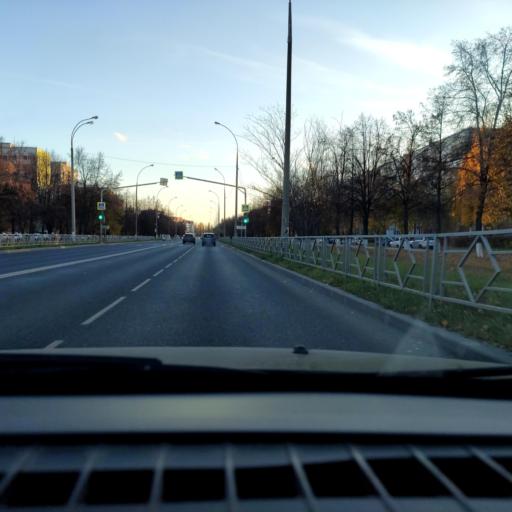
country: RU
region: Samara
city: Tol'yatti
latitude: 53.5222
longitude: 49.3108
